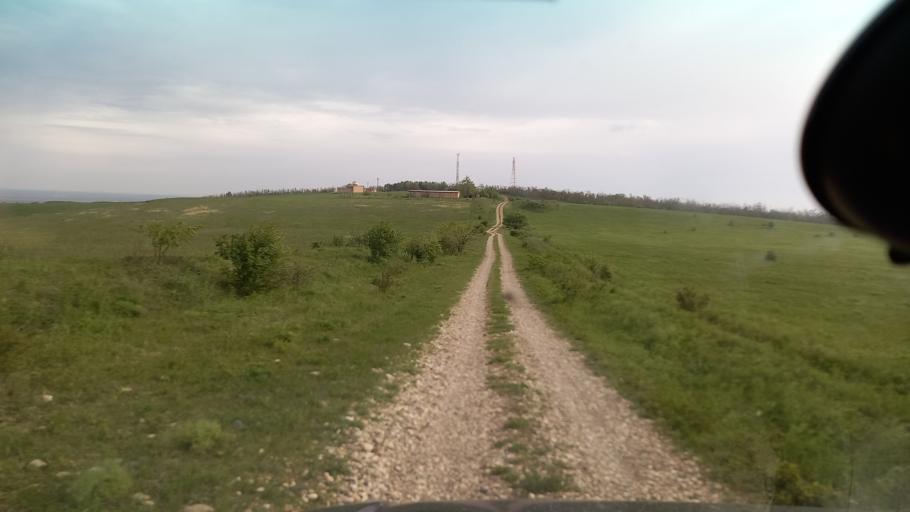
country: RU
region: Kabardino-Balkariya
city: Kuba-Taba
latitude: 43.8094
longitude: 43.4078
